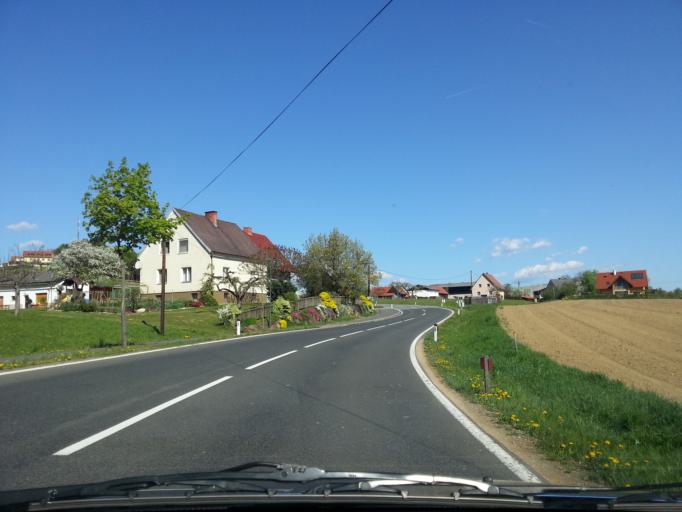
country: AT
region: Styria
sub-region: Politischer Bezirk Leibnitz
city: Arnfels
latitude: 46.6804
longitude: 15.3883
